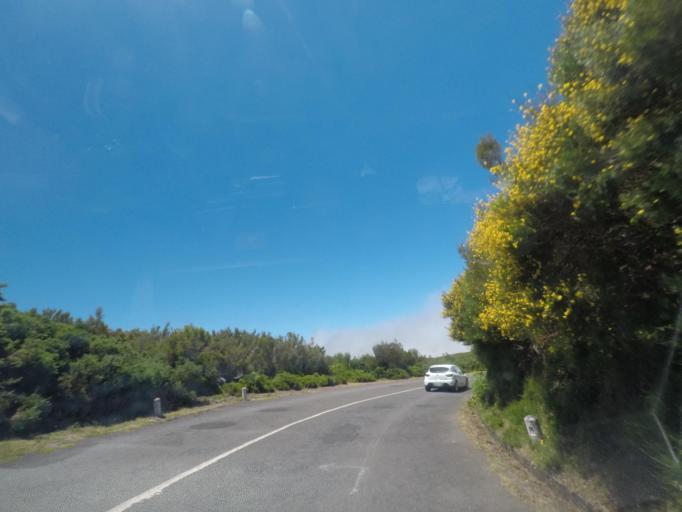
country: PT
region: Madeira
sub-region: Calheta
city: Faja da Ovelha
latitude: 32.8067
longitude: -17.1967
